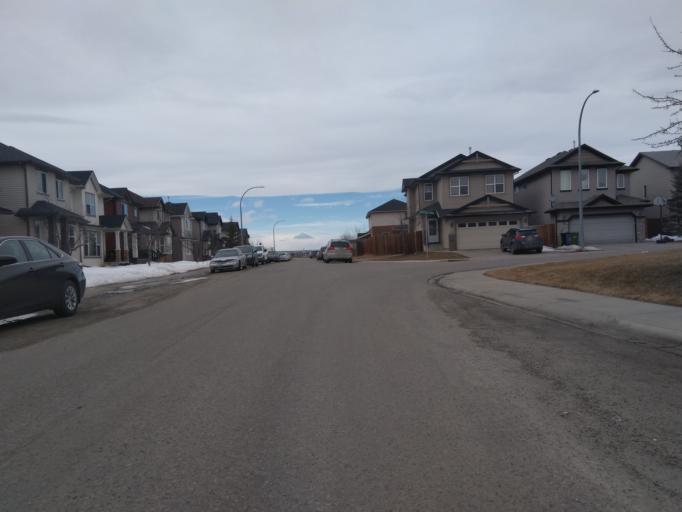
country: CA
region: Alberta
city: Chestermere
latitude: 51.1371
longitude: -113.9440
